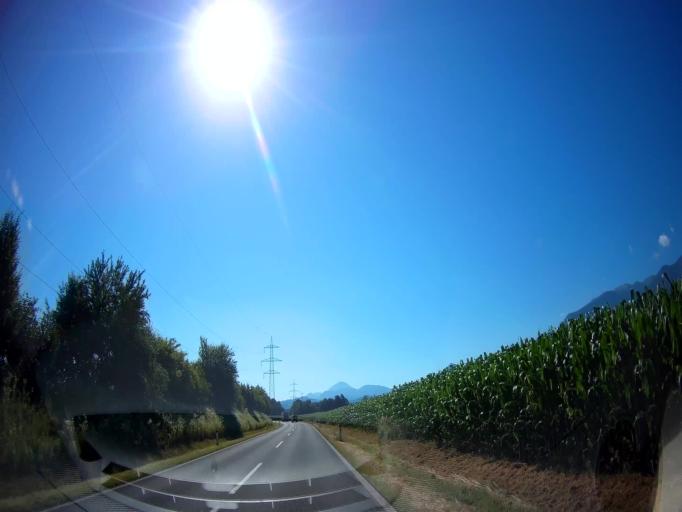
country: AT
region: Carinthia
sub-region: Politischer Bezirk Volkermarkt
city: Feistritz ob Bleiburg
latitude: 46.5744
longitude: 14.7445
